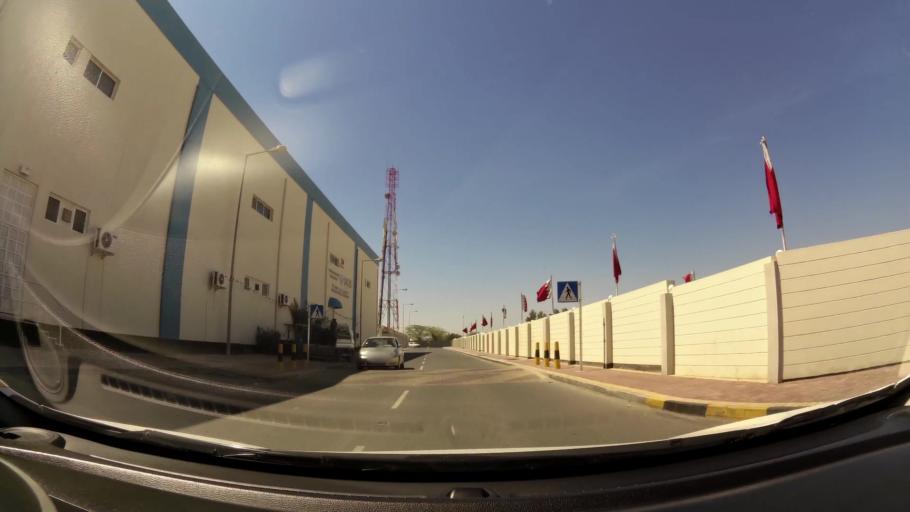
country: BH
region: Muharraq
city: Al Muharraq
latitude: 26.2686
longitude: 50.6148
